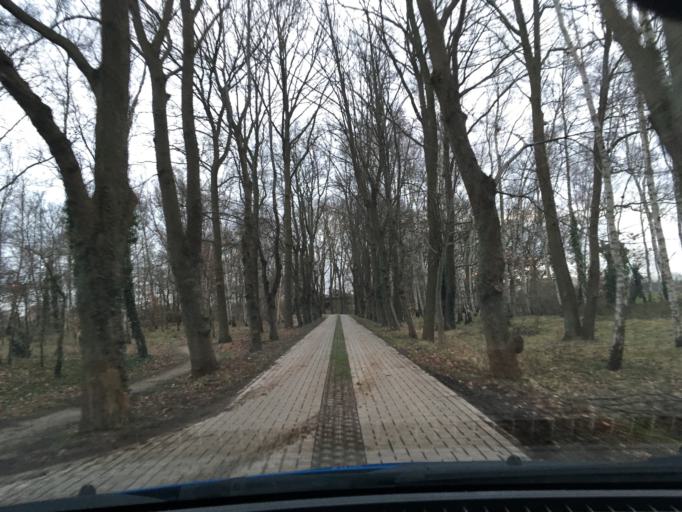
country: DE
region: Lower Saxony
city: Bardowick
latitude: 53.3055
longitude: 10.3780
